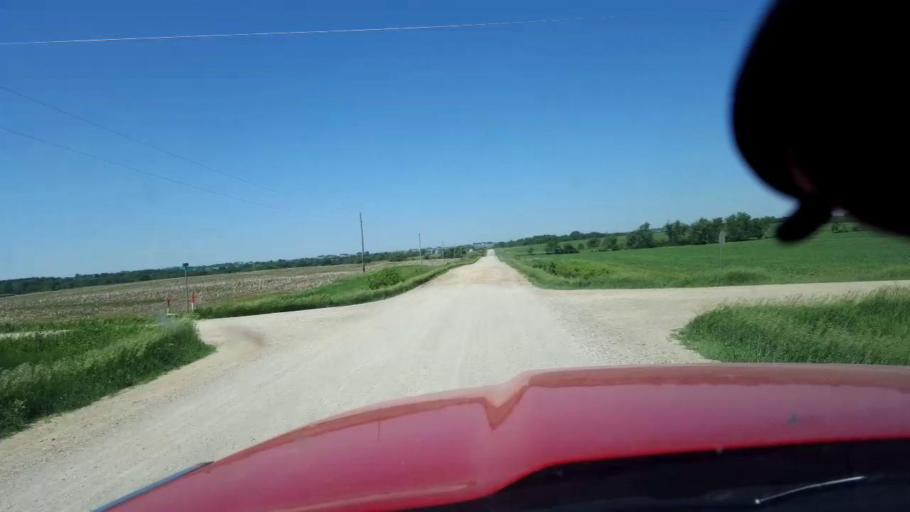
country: US
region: Iowa
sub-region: Chickasaw County
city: New Hampton
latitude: 43.2137
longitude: -92.2590
